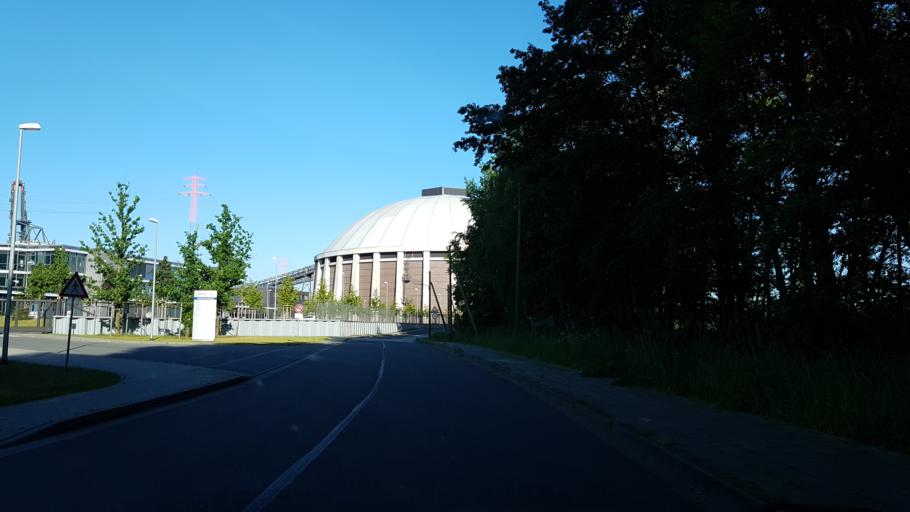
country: DE
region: Hamburg
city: Harburg
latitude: 53.4876
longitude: 9.9474
